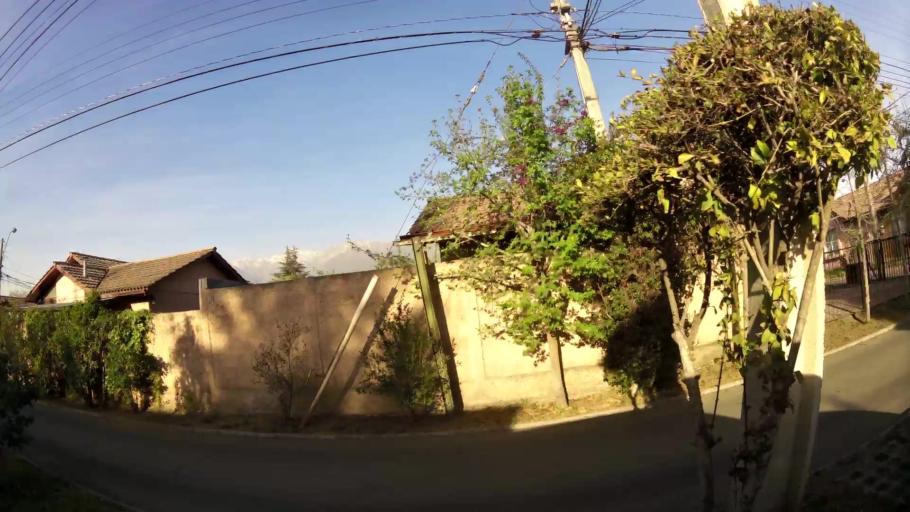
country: CL
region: Santiago Metropolitan
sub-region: Provincia de Cordillera
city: Puente Alto
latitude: -33.5427
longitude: -70.5766
